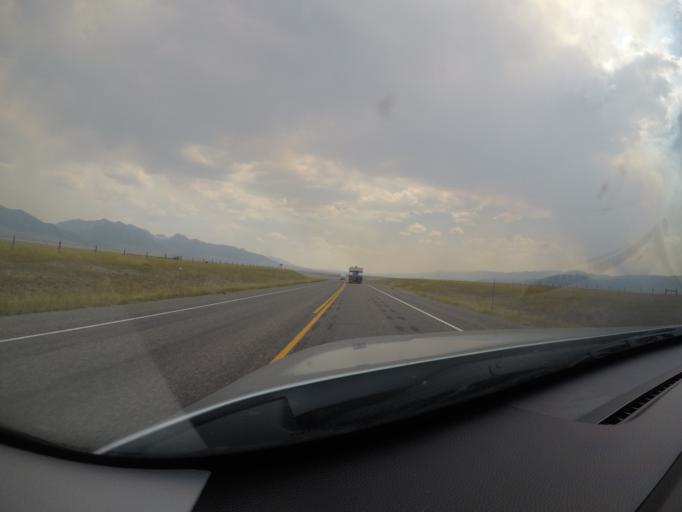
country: US
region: Montana
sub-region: Madison County
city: Virginia City
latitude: 45.1462
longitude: -111.6781
